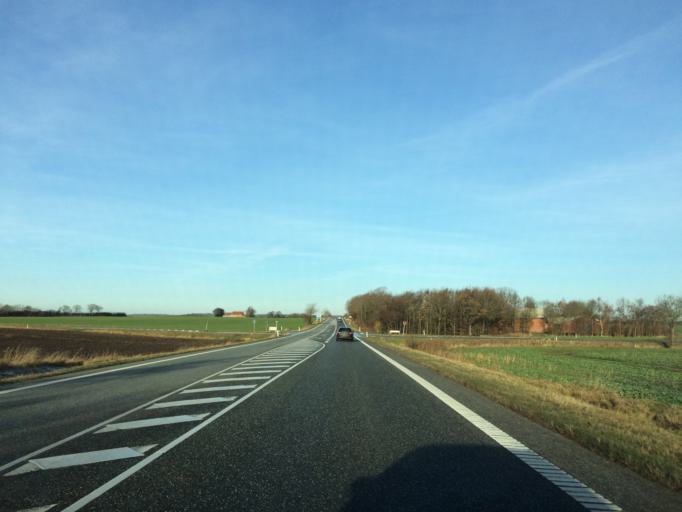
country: DK
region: South Denmark
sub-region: Fredericia Kommune
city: Taulov
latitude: 55.5697
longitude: 9.6665
